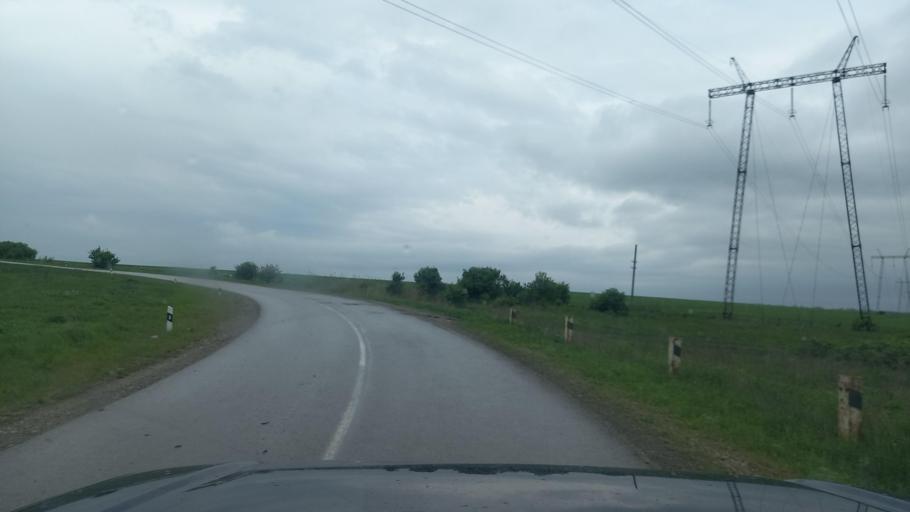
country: RU
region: Stavropol'skiy
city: Nevinnomyssk
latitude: 44.5902
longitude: 42.2246
